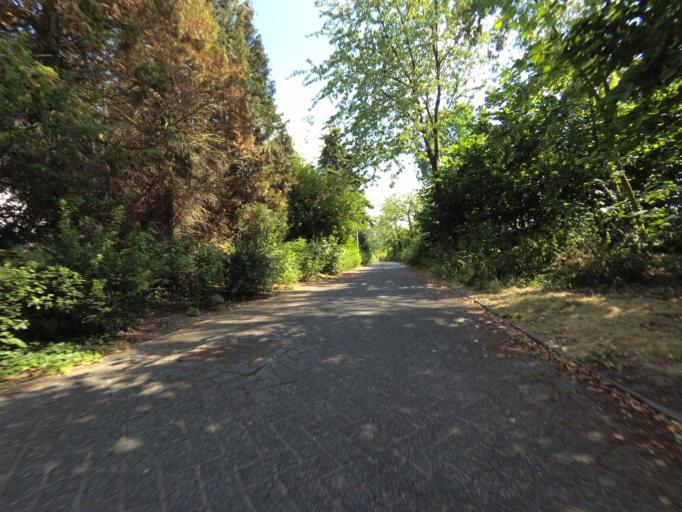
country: NL
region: Overijssel
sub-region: Gemeente Oldenzaal
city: Oldenzaal
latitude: 52.3231
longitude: 6.9218
